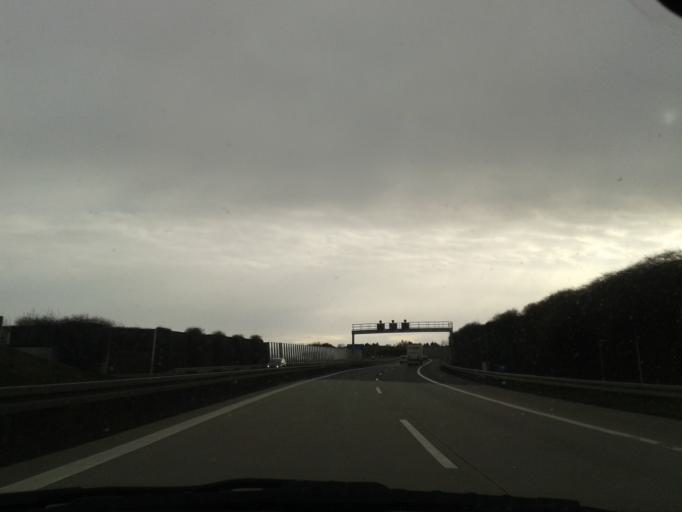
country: DE
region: Saxony
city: Freital
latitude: 51.0464
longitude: 13.6078
